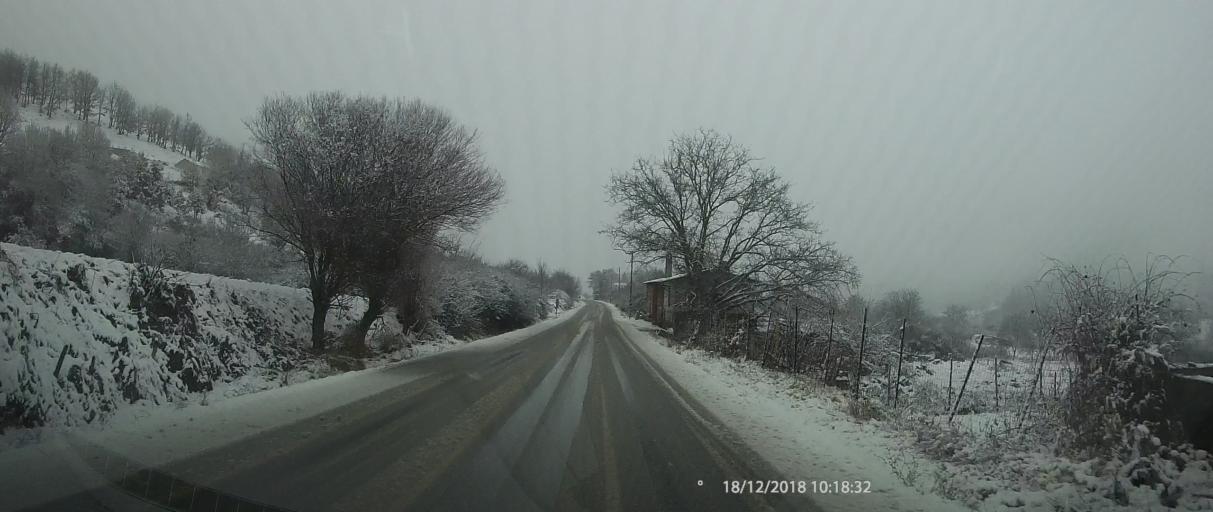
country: GR
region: Thessaly
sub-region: Nomos Larisis
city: Livadi
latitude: 40.1324
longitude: 22.2177
